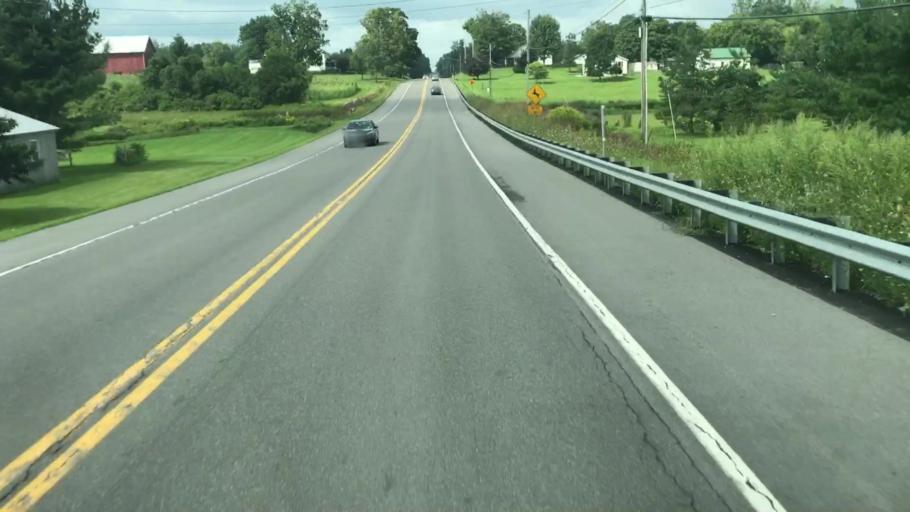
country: US
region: New York
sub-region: Onondaga County
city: Skaneateles
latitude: 42.9411
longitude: -76.4854
